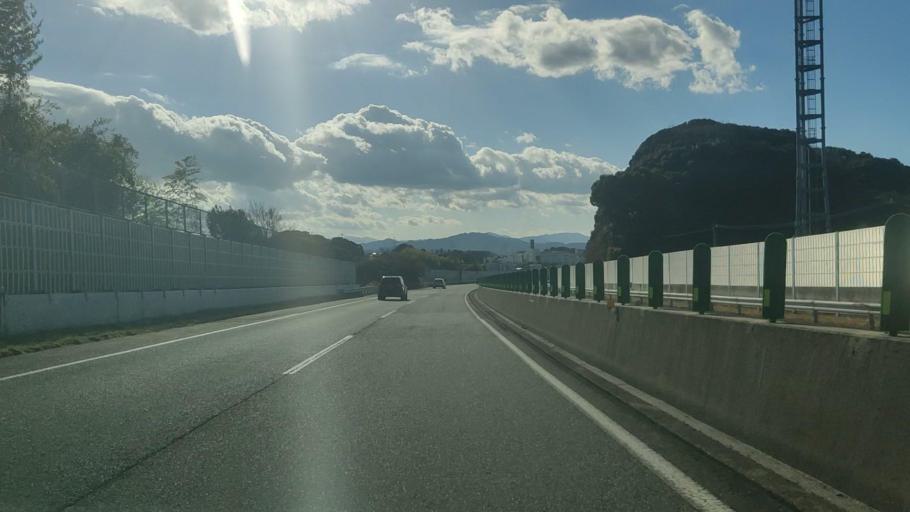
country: JP
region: Fukuoka
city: Nakama
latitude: 33.8233
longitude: 130.7614
